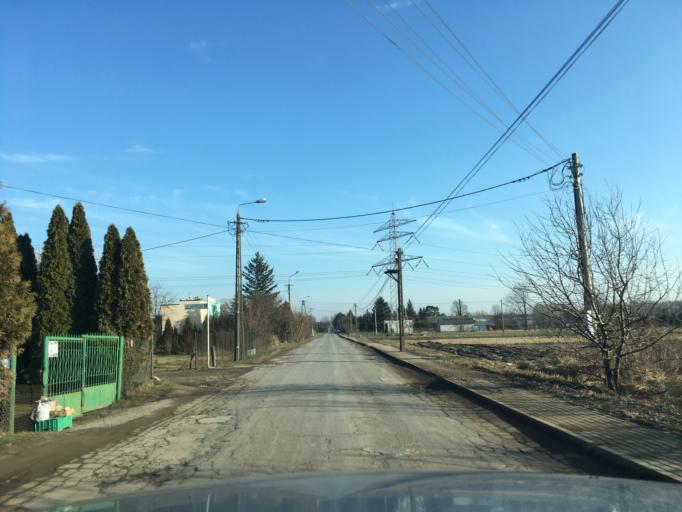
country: PL
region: Masovian Voivodeship
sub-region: Powiat piaseczynski
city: Lesznowola
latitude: 52.0568
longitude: 20.8774
